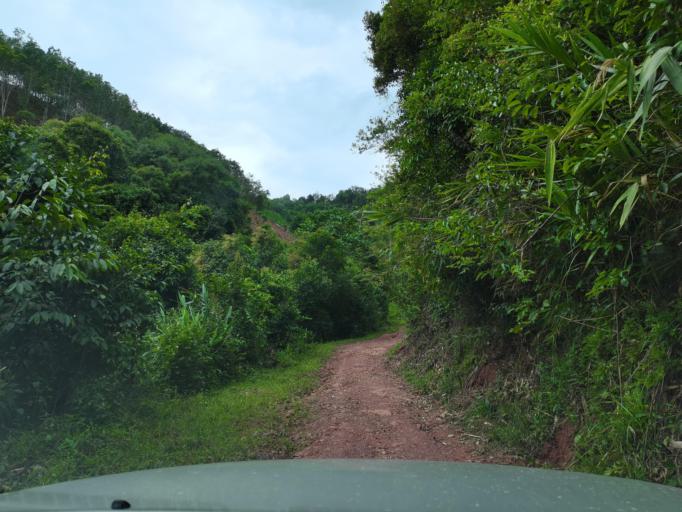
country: LA
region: Loungnamtha
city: Muang Nale
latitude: 20.5058
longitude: 101.0853
